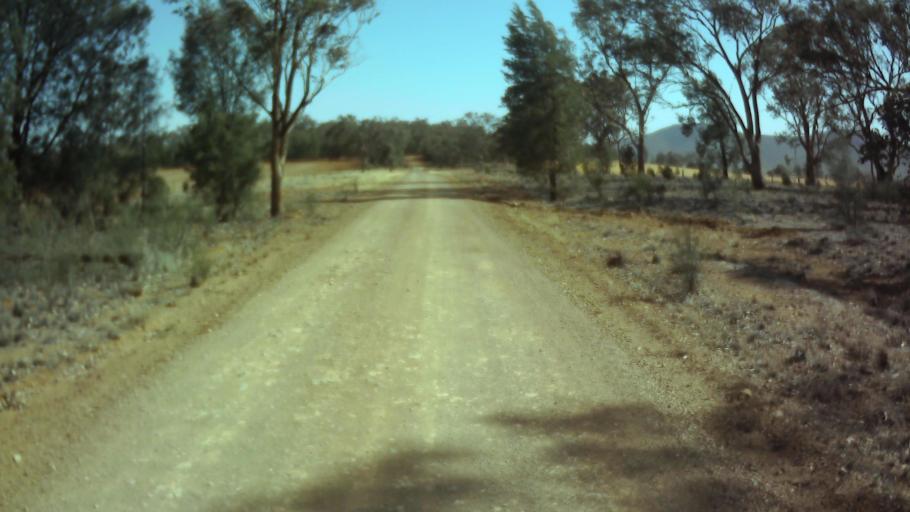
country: AU
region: New South Wales
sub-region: Weddin
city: Grenfell
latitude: -33.8578
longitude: 148.0155
